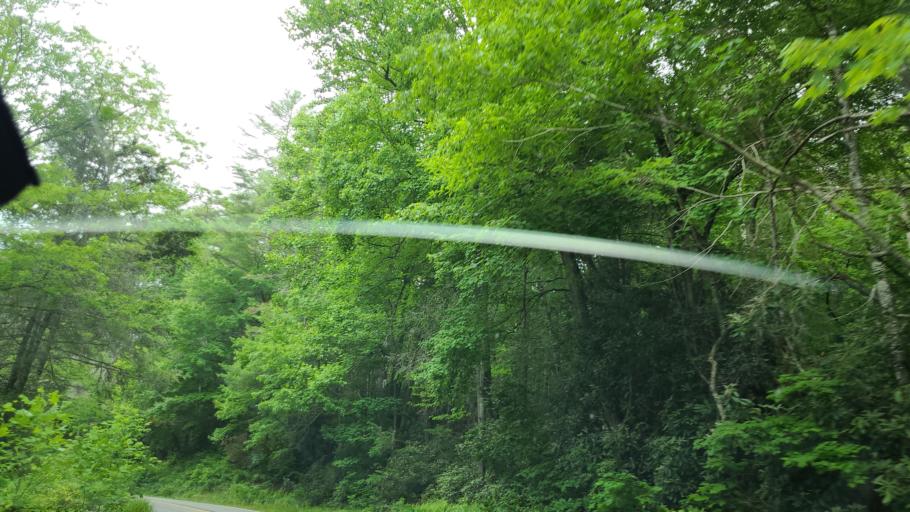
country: US
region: North Carolina
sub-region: Macon County
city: Franklin
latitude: 35.0777
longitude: -83.2507
